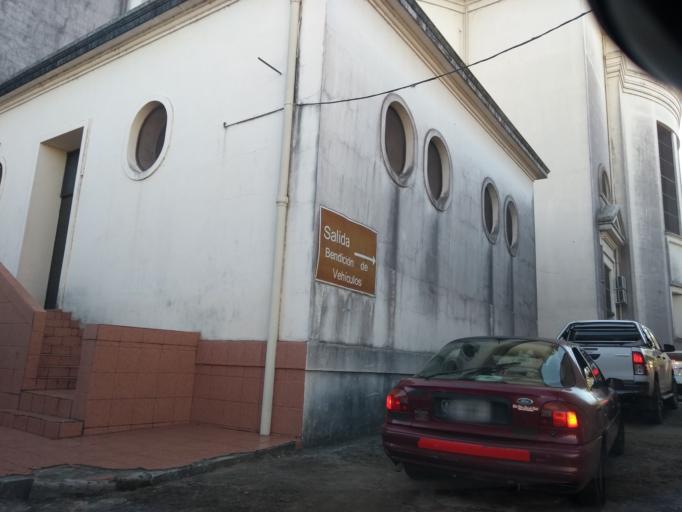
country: AR
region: Corrientes
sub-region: Departamento de Itati
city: Itati
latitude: -27.2695
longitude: -58.2442
